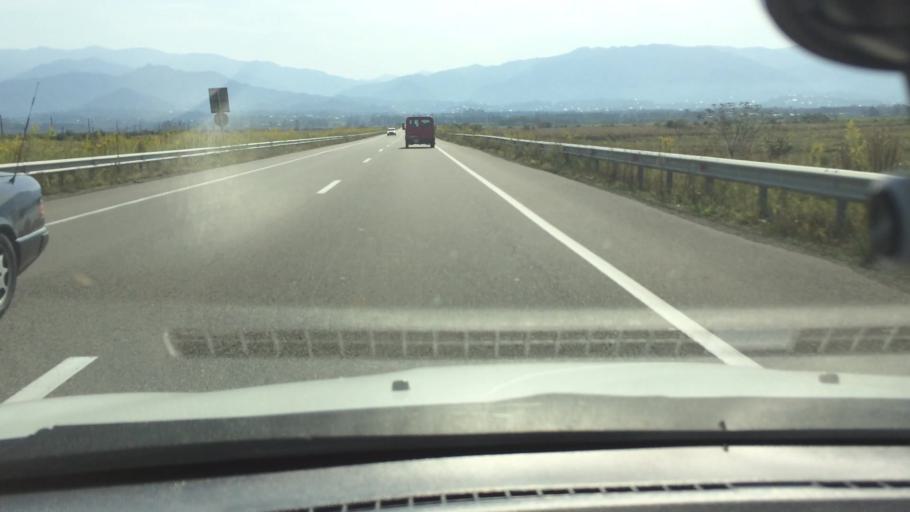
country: GE
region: Ajaria
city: Ochkhamuri
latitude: 41.8769
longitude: 41.8237
